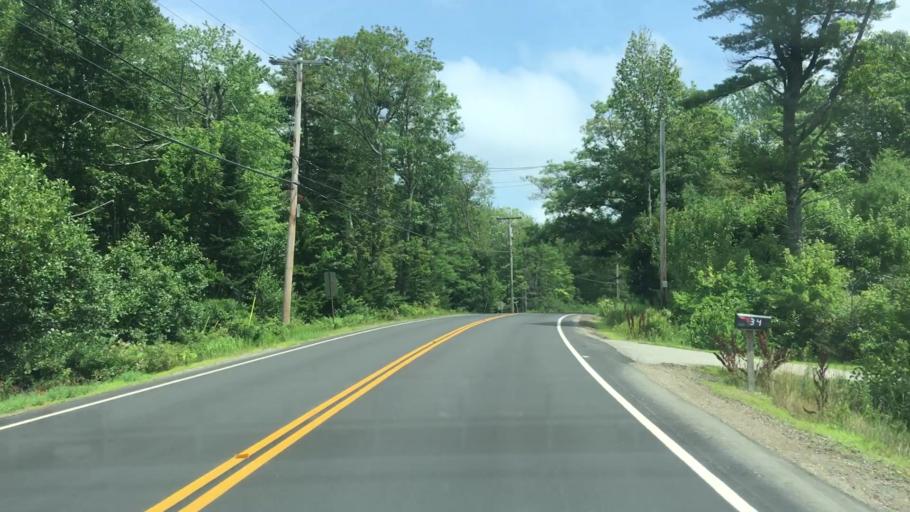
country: US
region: Maine
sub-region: Cumberland County
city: Brunswick
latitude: 43.8488
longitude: -69.9101
